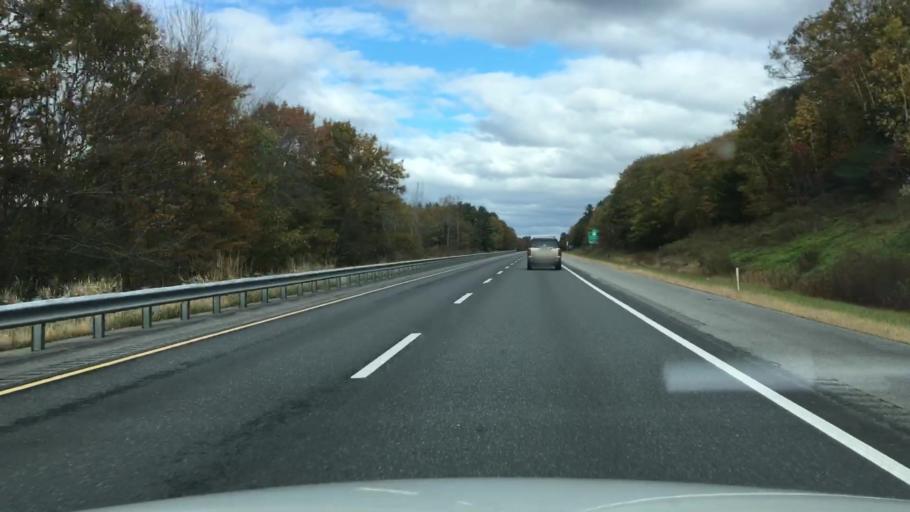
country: US
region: Maine
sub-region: Sagadahoc County
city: Richmond
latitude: 44.0776
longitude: -69.8776
